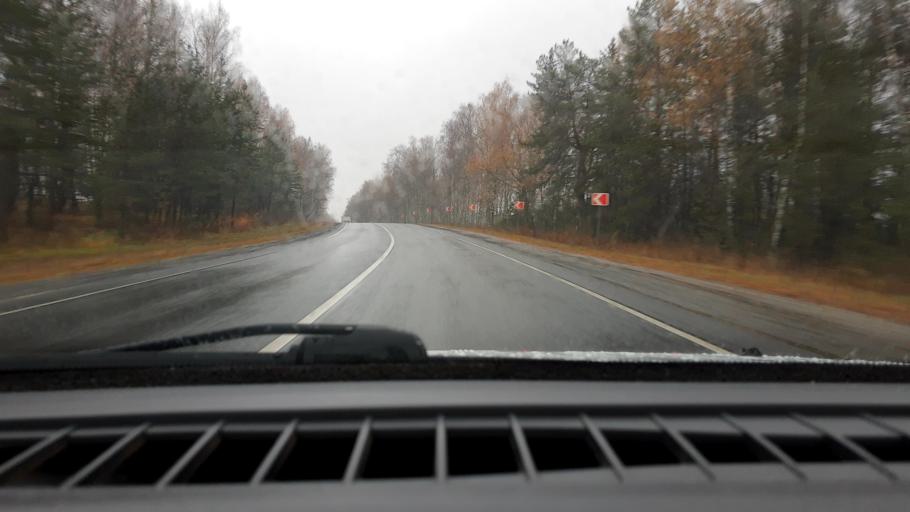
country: RU
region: Nizjnij Novgorod
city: Linda
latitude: 56.6762
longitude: 44.1454
